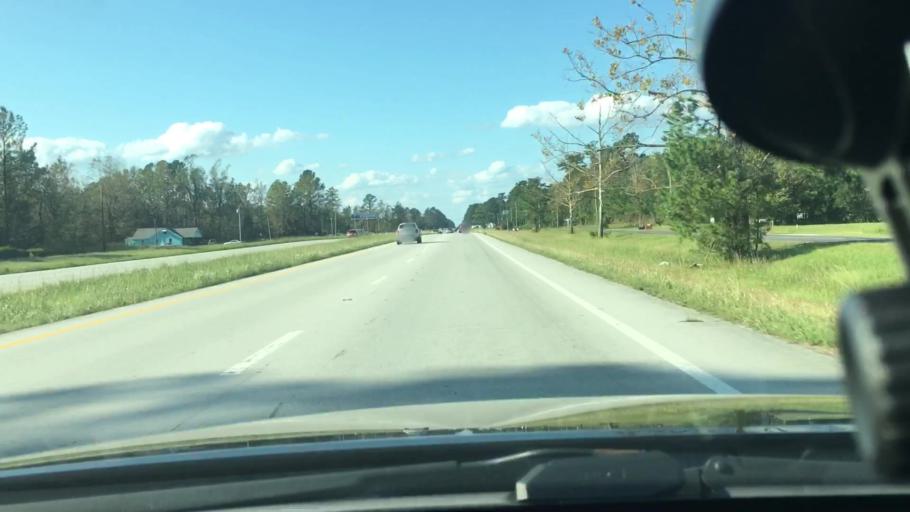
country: US
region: North Carolina
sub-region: Craven County
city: Neuse Forest
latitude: 35.0062
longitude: -76.9898
